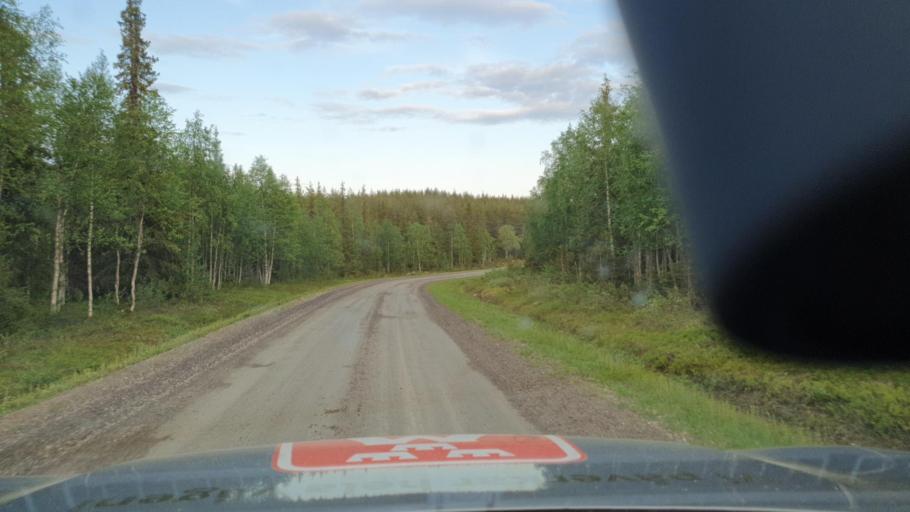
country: SE
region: Norrbotten
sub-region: Bodens Kommun
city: Boden
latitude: 66.5176
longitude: 21.5188
